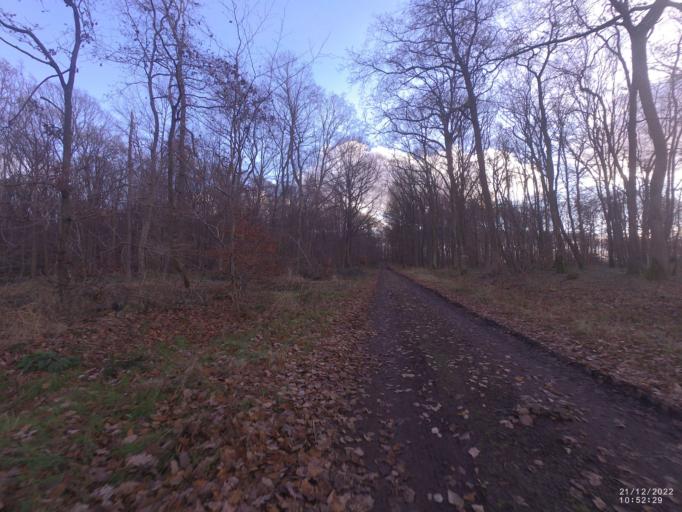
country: DE
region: Rheinland-Pfalz
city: Konigsfeld
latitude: 50.4981
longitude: 7.1911
